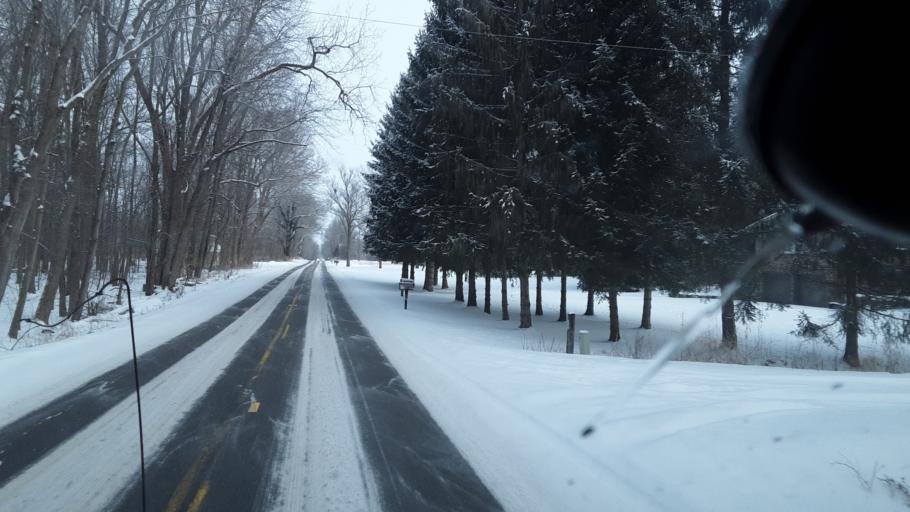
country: US
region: Michigan
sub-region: Jackson County
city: Jackson
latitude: 42.3128
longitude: -84.4829
